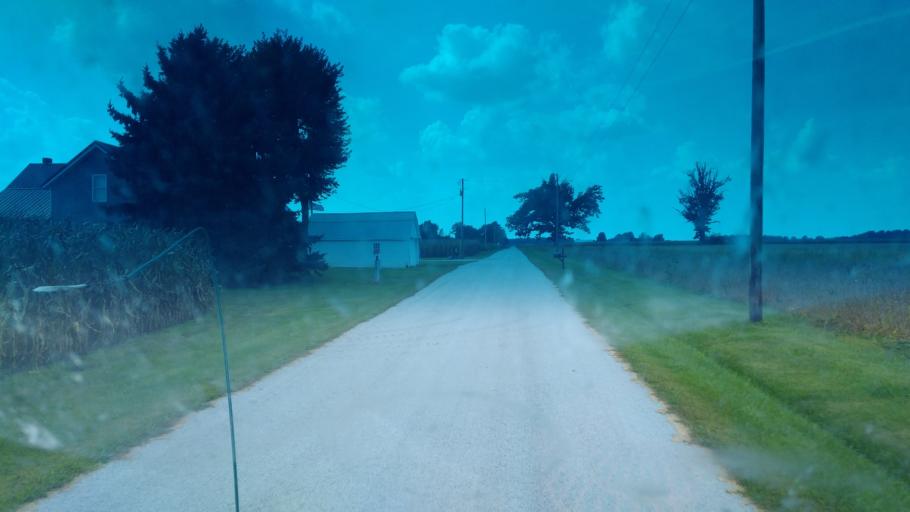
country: US
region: Ohio
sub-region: Hardin County
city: Kenton
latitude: 40.6893
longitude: -83.7188
